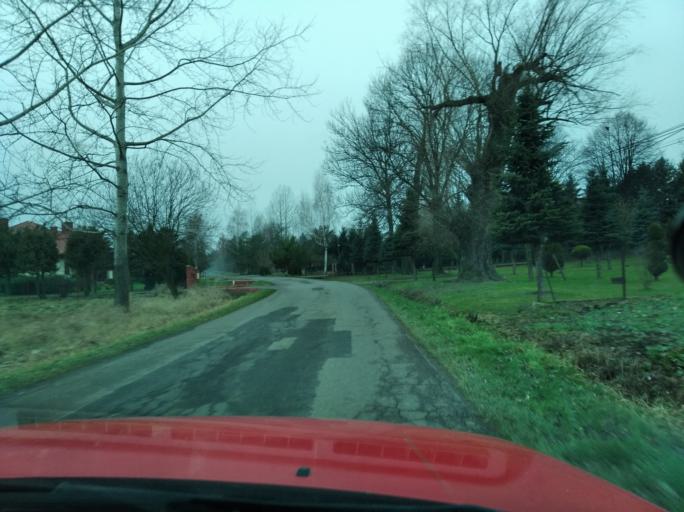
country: PL
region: Subcarpathian Voivodeship
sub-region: Powiat jaroslawski
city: Wierzbna
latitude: 50.0165
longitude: 22.6170
